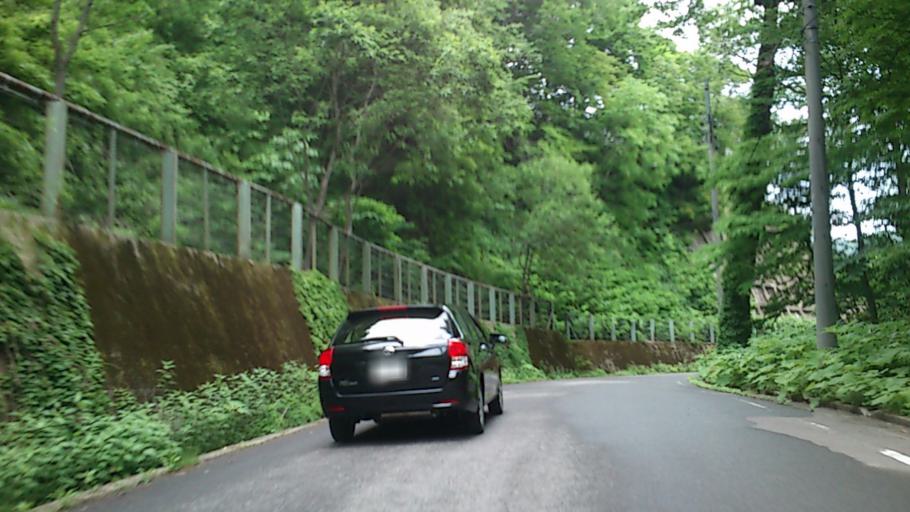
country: JP
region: Aomori
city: Hirosaki
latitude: 40.5164
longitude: 140.1788
